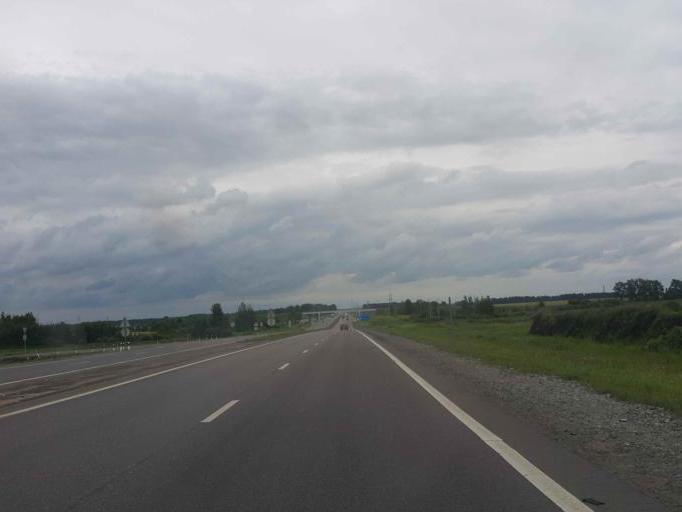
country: RU
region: Tambov
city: Zavoronezhskoye
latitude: 52.8903
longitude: 40.7000
